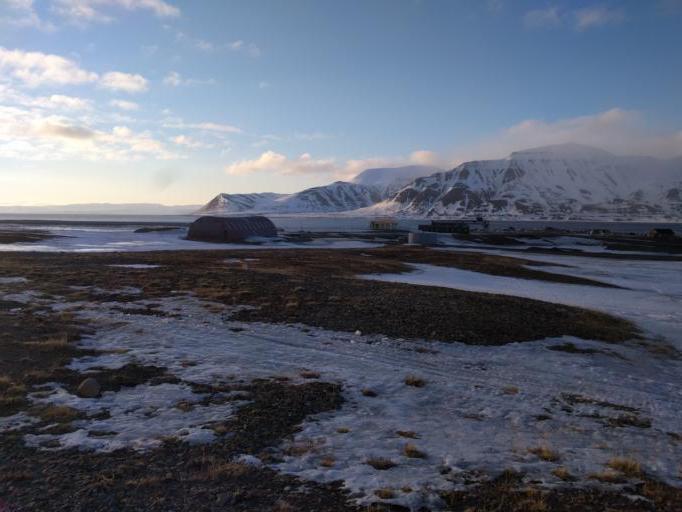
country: SJ
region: Svalbard
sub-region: Spitsbergen
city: Longyearbyen
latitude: 78.2410
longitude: 15.5134
